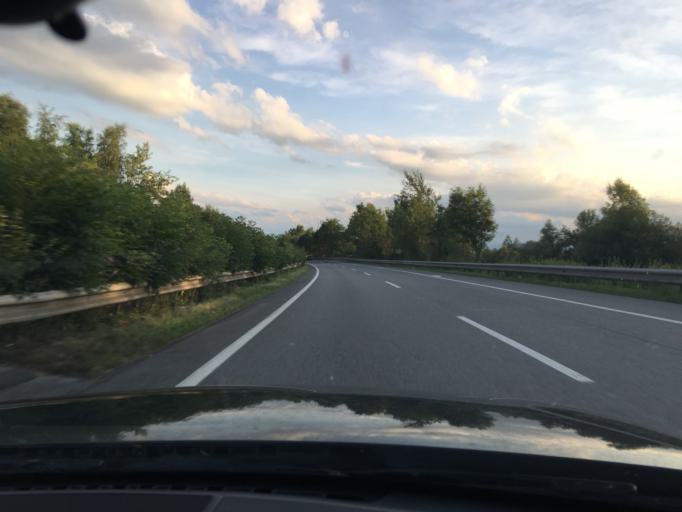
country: AT
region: Vorarlberg
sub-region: Politischer Bezirk Bregenz
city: Lauterach
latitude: 47.4601
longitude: 9.7237
